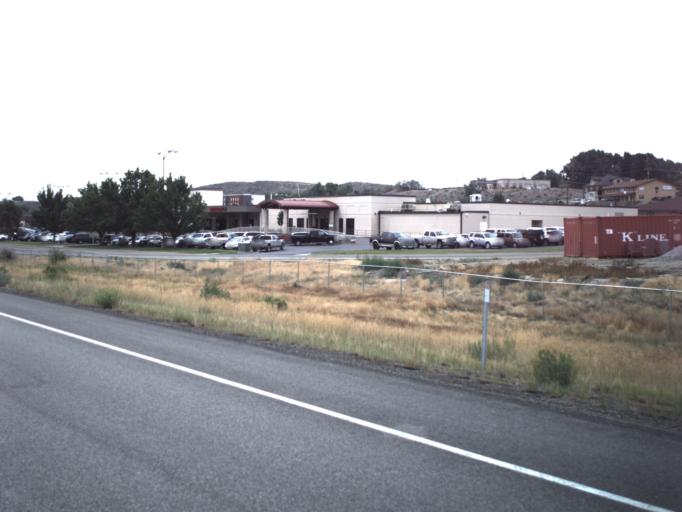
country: US
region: Utah
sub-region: Carbon County
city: Carbonville
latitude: 39.6071
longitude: -110.8326
